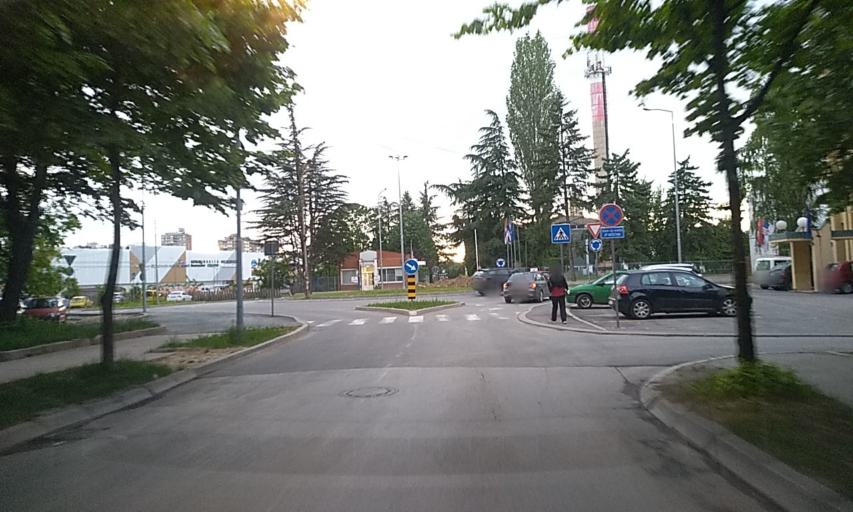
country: RS
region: Central Serbia
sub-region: Nisavski Okrug
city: Nis
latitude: 43.3243
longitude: 21.9153
